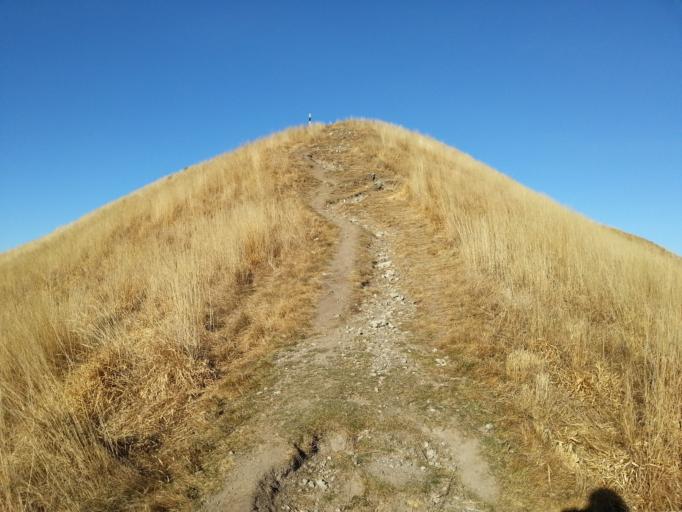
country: CH
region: Ticino
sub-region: Lugano District
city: Cadro
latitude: 46.0293
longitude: 9.0082
